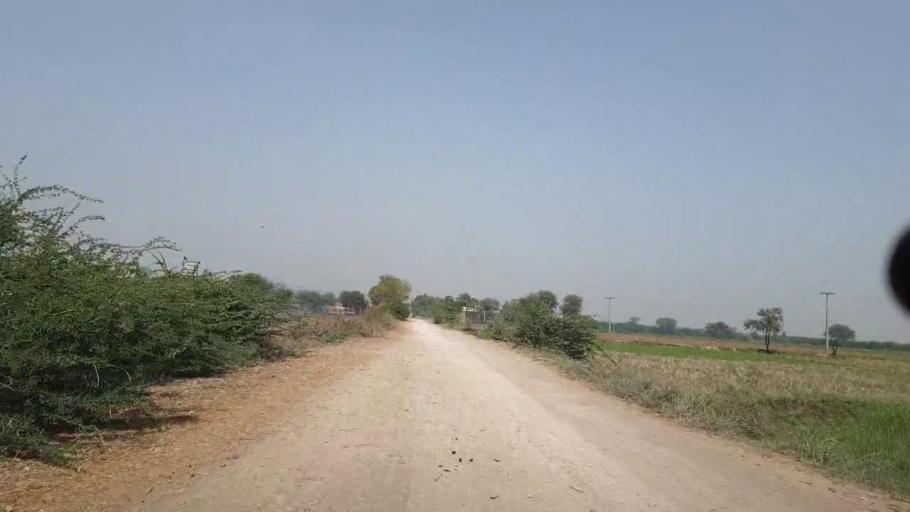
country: PK
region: Sindh
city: Matli
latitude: 25.0602
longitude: 68.7074
